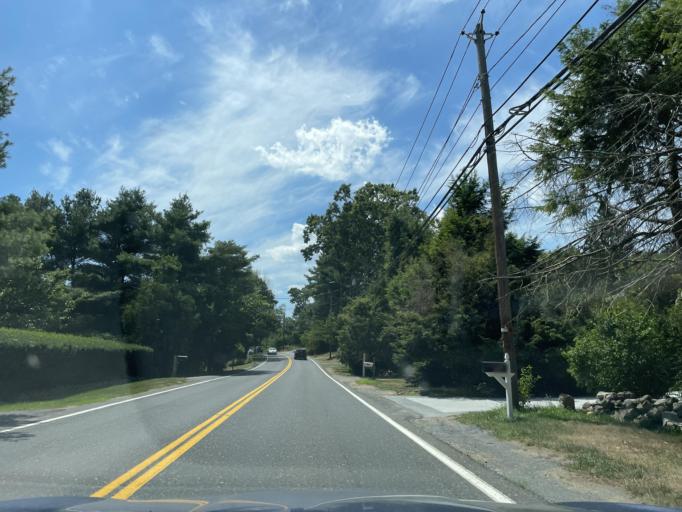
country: US
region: Massachusetts
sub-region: Middlesex County
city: Natick
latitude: 42.2585
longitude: -71.3347
